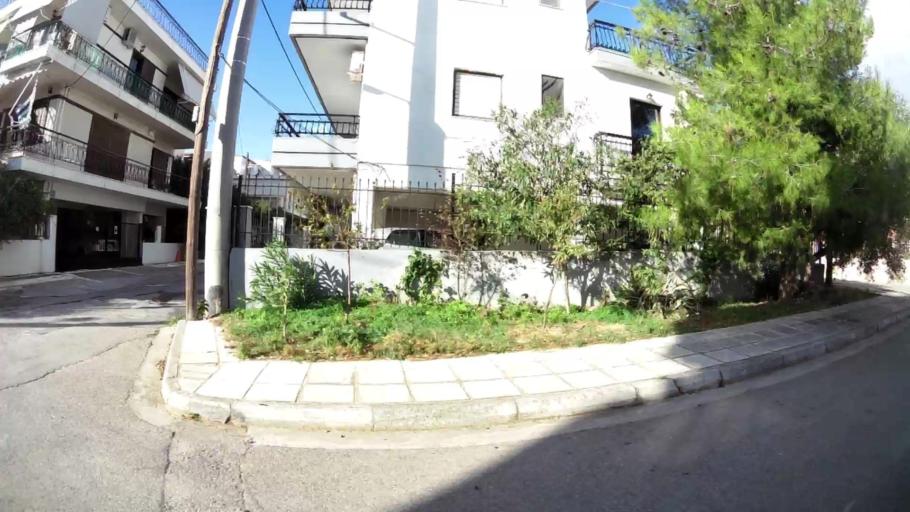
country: GR
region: Attica
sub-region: Nomarchia Anatolikis Attikis
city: Acharnes
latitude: 38.0700
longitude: 23.7428
